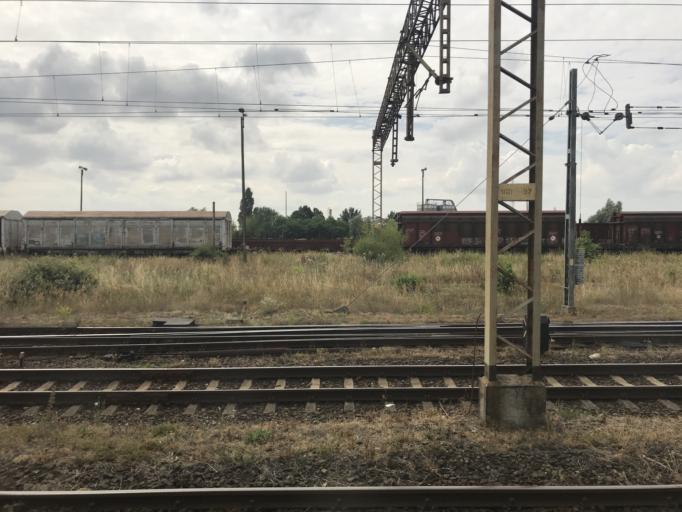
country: PL
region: Greater Poland Voivodeship
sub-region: Powiat gnieznienski
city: Gniezno
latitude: 52.5305
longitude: 17.6150
